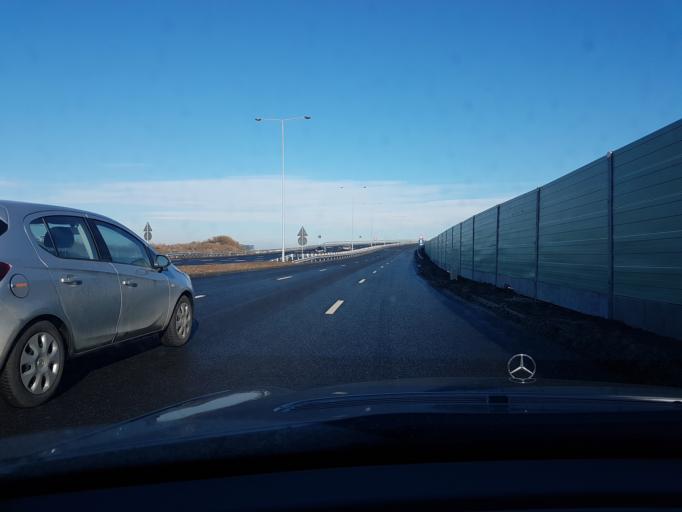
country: RO
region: Ilfov
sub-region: Comuna Fundeni-Dobroesti
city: Fundeni
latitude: 44.4796
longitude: 26.1381
